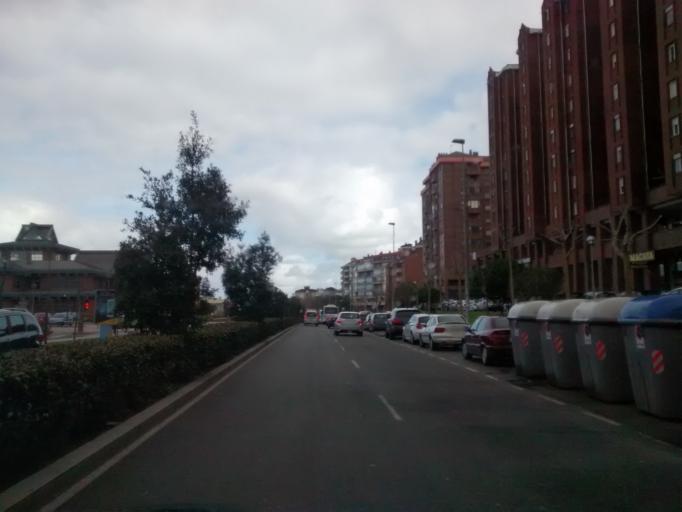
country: ES
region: Cantabria
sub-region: Provincia de Cantabria
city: Santander
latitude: 43.4700
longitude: -3.8068
